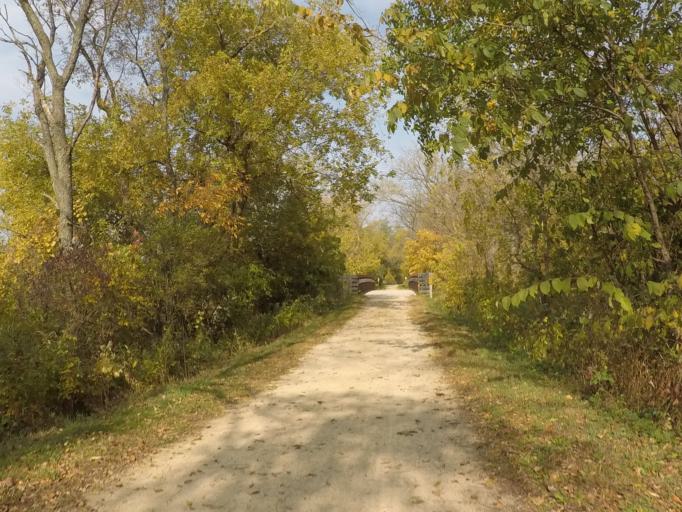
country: US
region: Wisconsin
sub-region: Iowa County
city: Barneveld
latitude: 43.0166
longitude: -89.8285
